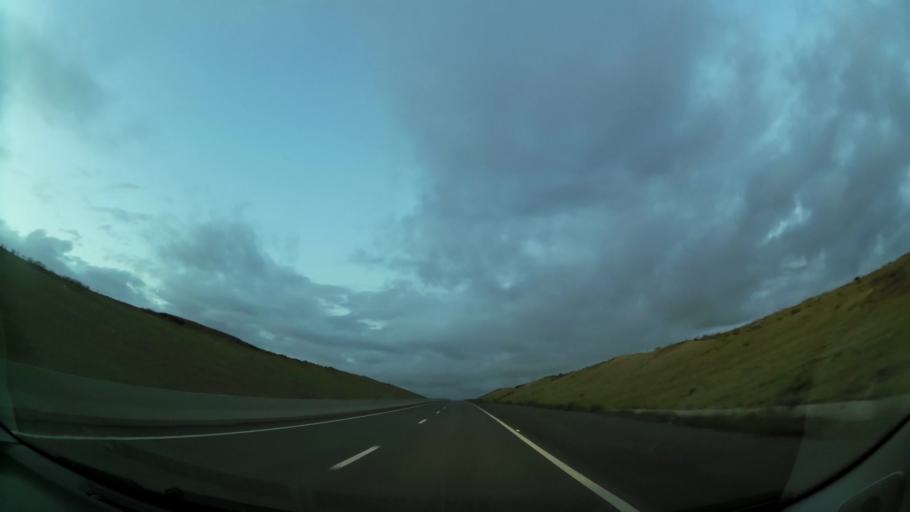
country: MA
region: Oriental
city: El Aioun
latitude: 34.6174
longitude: -2.4079
